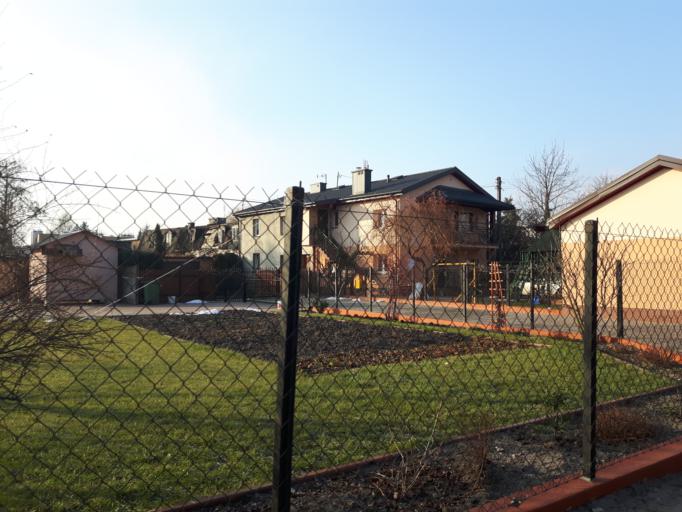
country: PL
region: Masovian Voivodeship
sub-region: Powiat wolominski
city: Zabki
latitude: 52.2884
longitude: 21.1027
